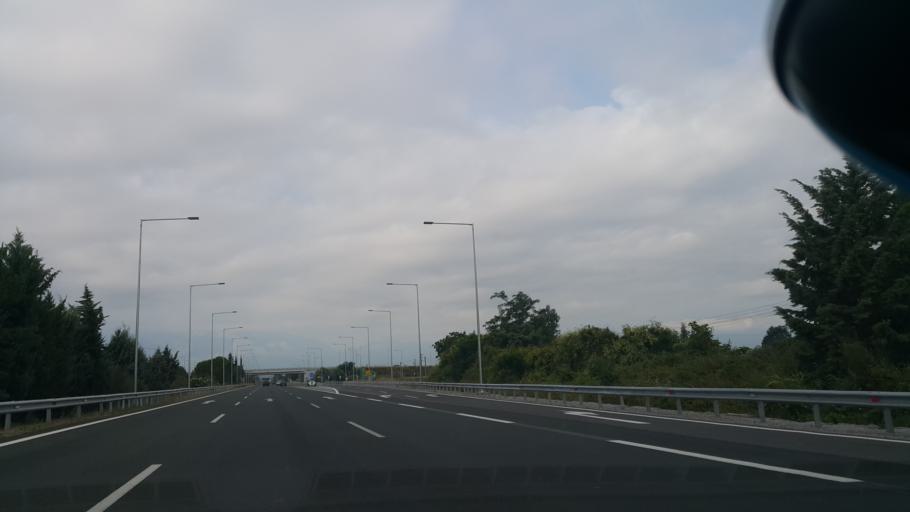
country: GR
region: Central Macedonia
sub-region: Nomos Pierias
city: Peristasi
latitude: 40.2919
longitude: 22.5374
